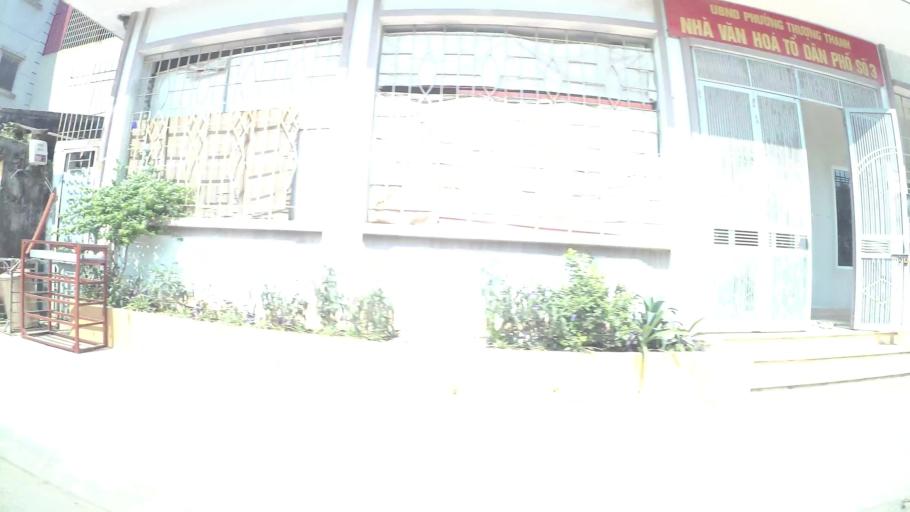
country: VN
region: Ha Noi
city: Hoan Kiem
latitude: 21.0546
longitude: 105.8771
